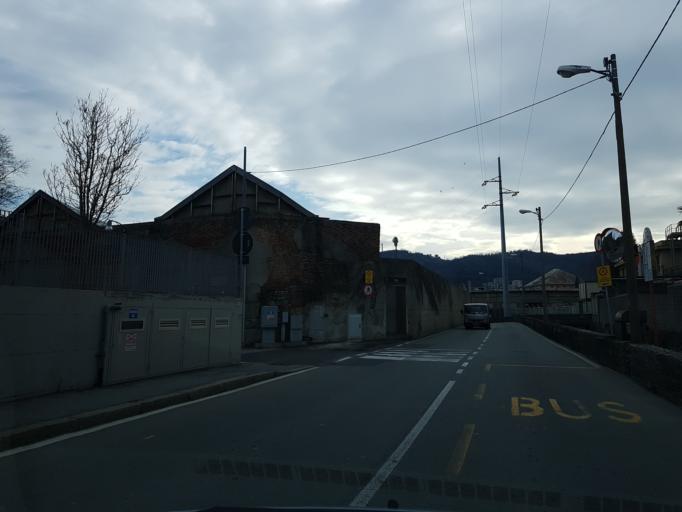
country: IT
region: Liguria
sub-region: Provincia di Genova
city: Genoa
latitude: 44.4375
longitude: 8.8834
